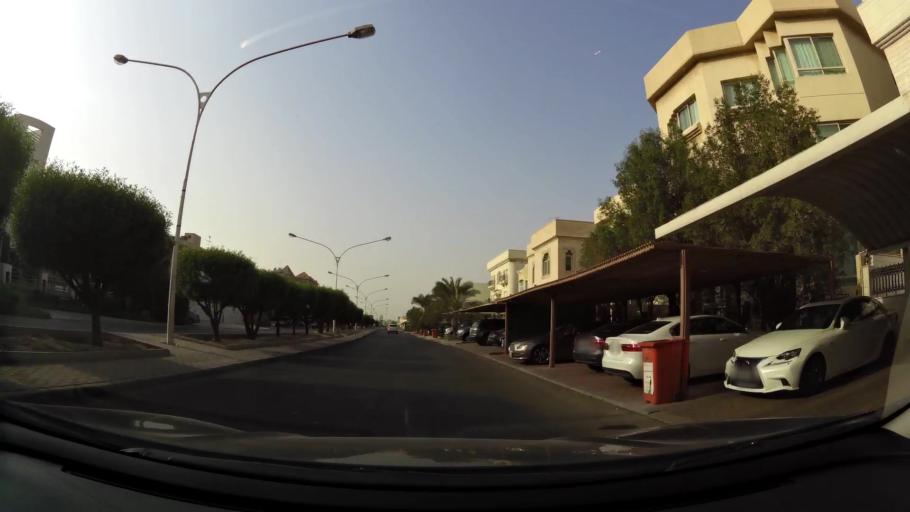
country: KW
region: Muhafazat Hawalli
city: Hawalli
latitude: 29.3103
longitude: 48.0081
